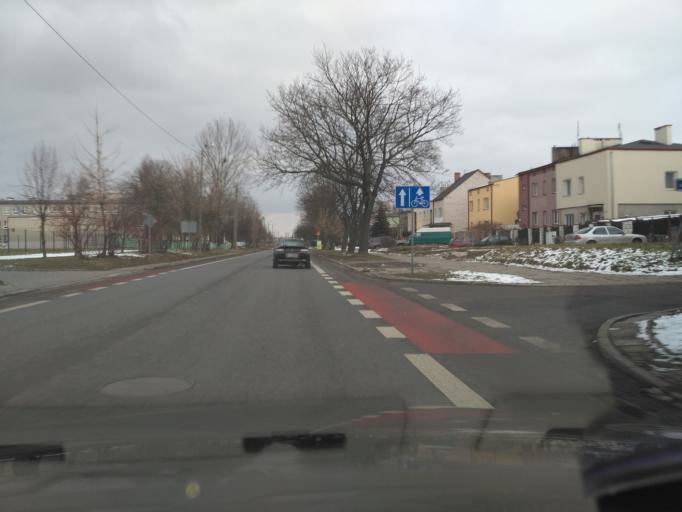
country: PL
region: Lublin Voivodeship
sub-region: Powiat lubelski
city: Lublin
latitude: 51.2306
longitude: 22.5974
